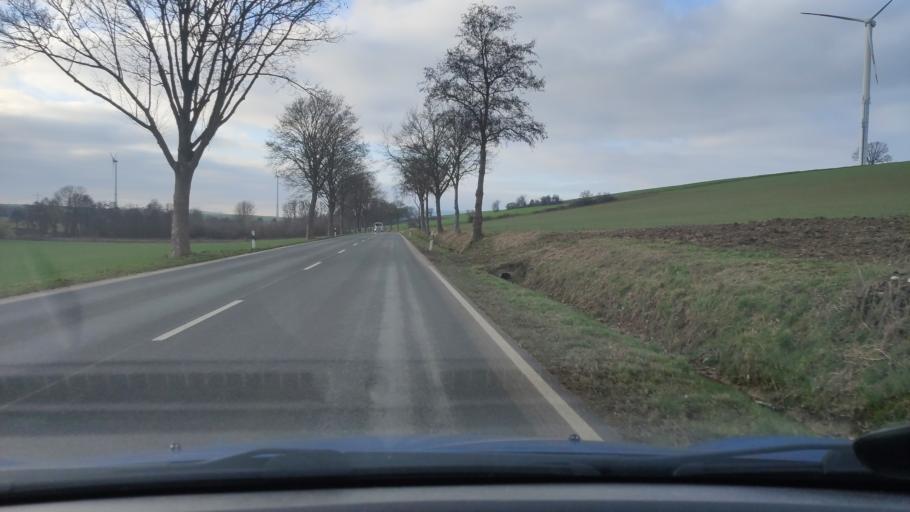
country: DE
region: Lower Saxony
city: Coppenbrugge
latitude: 52.1357
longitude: 9.5333
